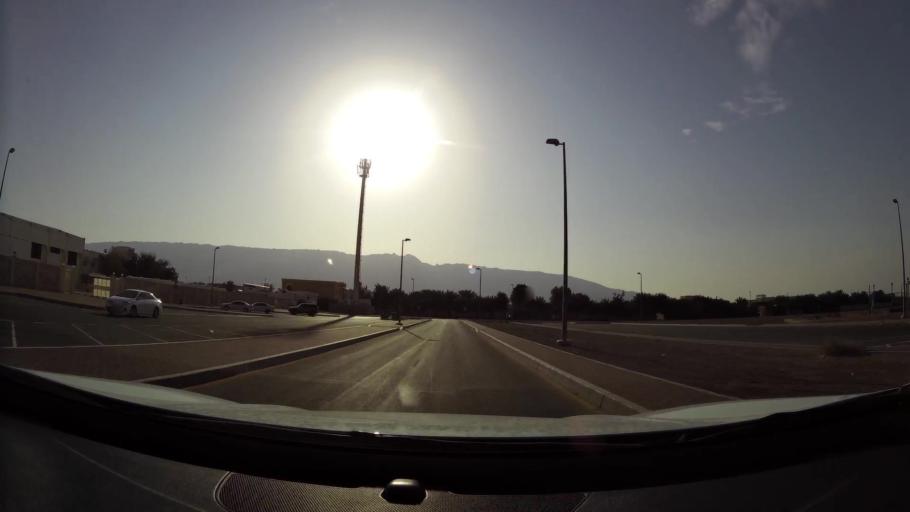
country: AE
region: Abu Dhabi
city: Al Ain
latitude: 24.0771
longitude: 55.8413
